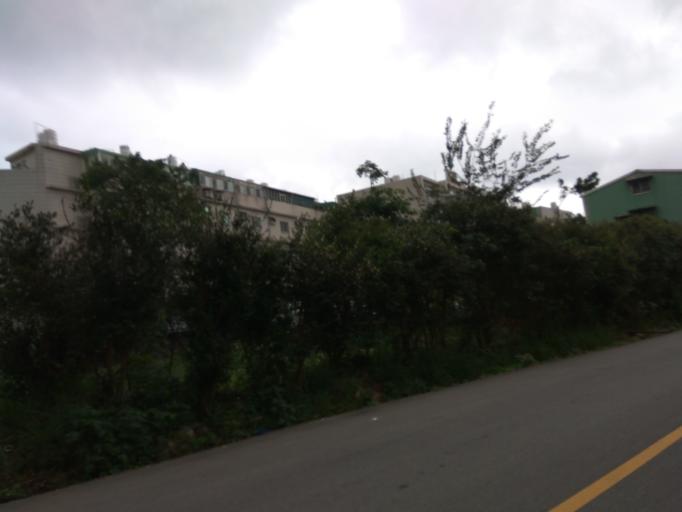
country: TW
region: Taiwan
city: Taoyuan City
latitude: 24.9868
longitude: 121.2286
